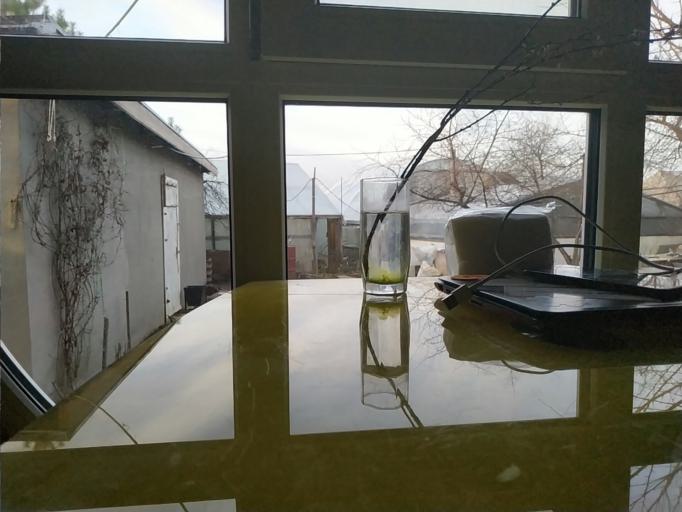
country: RU
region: Republic of Karelia
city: Suoyarvi
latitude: 62.2306
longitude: 32.1043
